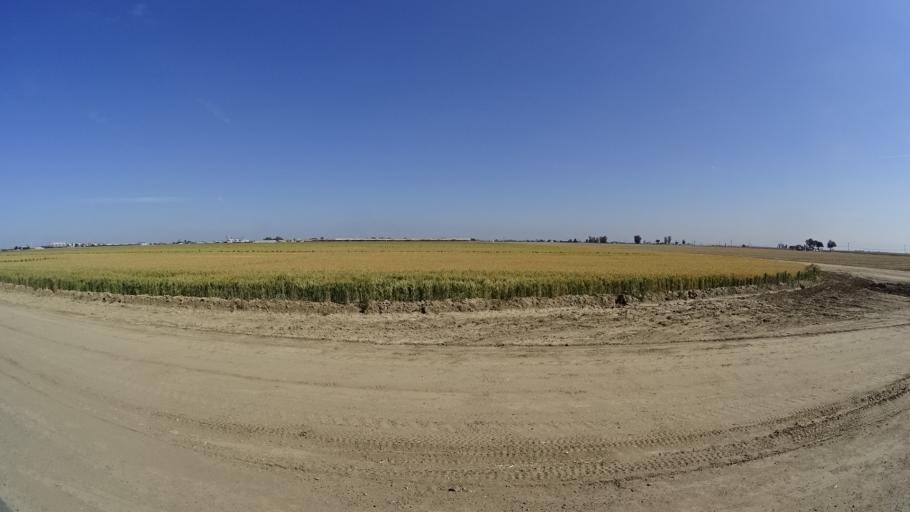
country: US
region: California
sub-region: Kings County
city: Home Garden
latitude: 36.2549
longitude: -119.6239
